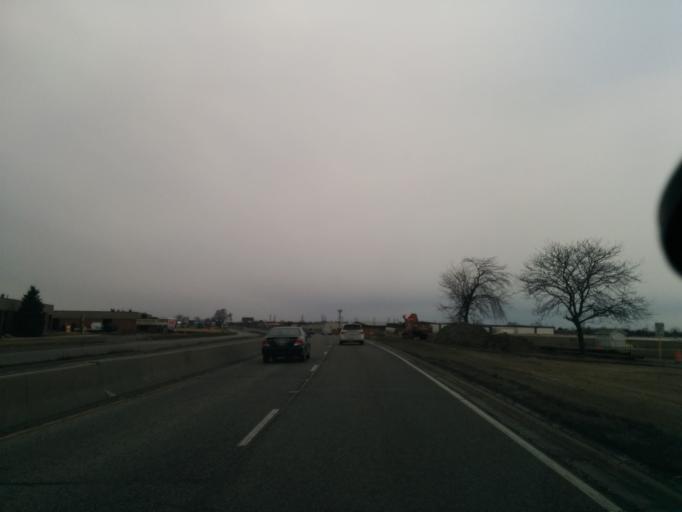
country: US
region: Illinois
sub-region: Cook County
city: Prospect Heights
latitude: 42.1092
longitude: -87.8973
